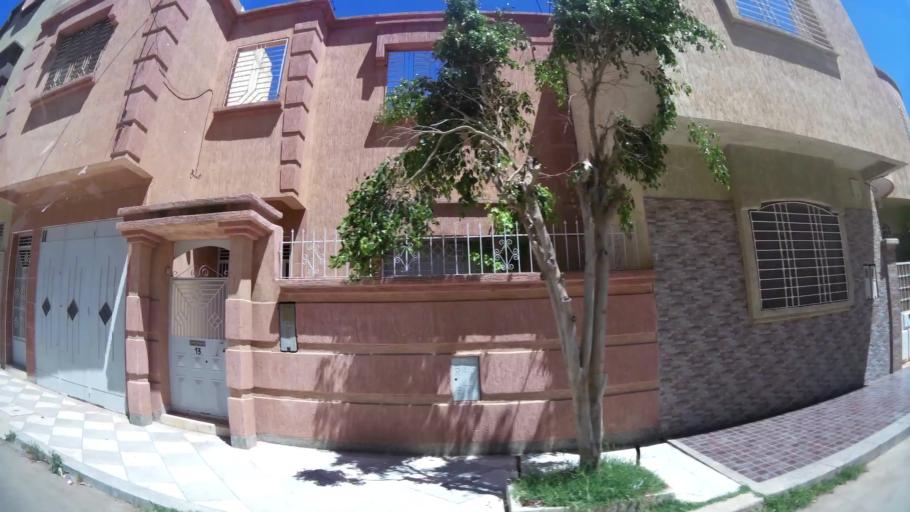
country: MA
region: Oriental
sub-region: Oujda-Angad
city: Oujda
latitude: 34.6666
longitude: -1.8864
